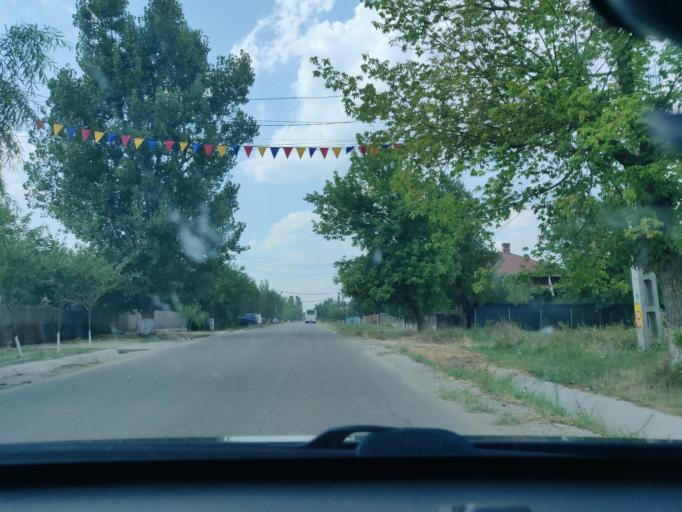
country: RO
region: Teleorman
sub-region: Comuna Sarbeni
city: Sarbeni
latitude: 44.4660
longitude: 25.3883
